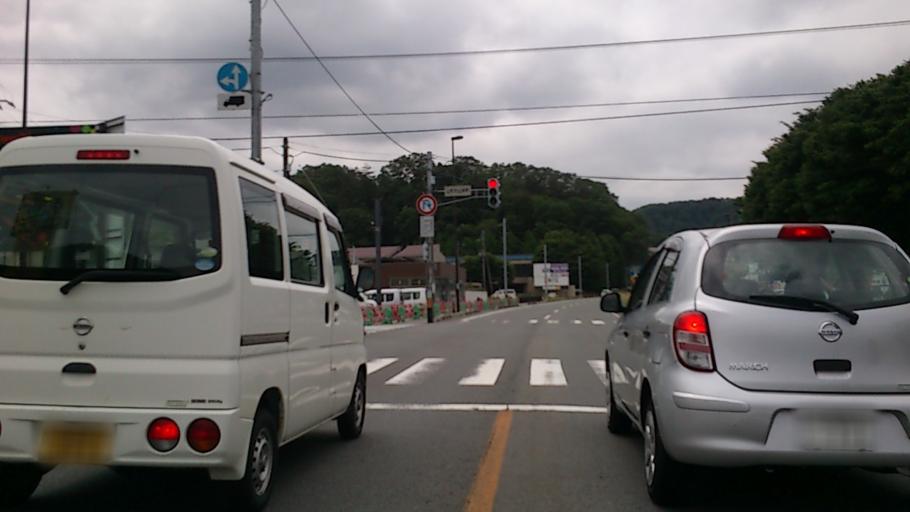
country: JP
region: Yamagata
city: Yamagata-shi
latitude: 38.2656
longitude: 140.3622
